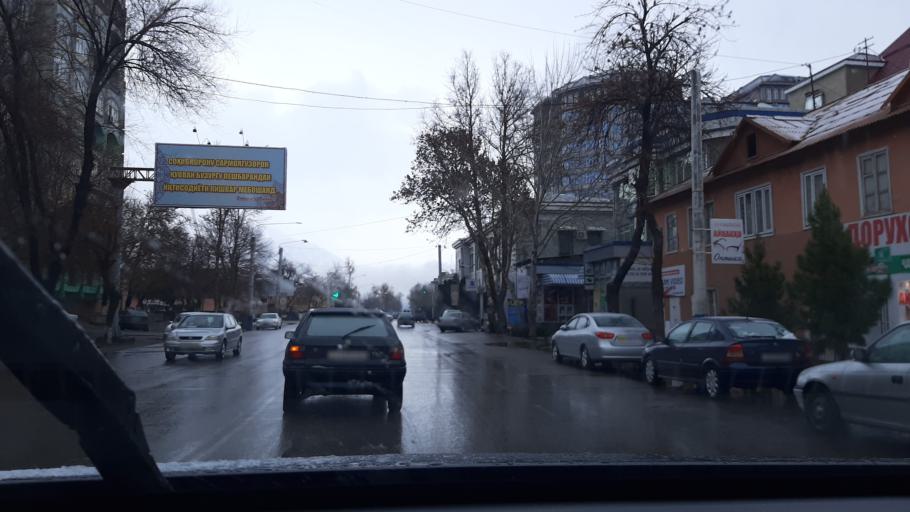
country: TJ
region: Viloyati Sughd
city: Khujand
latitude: 40.2767
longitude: 69.6410
